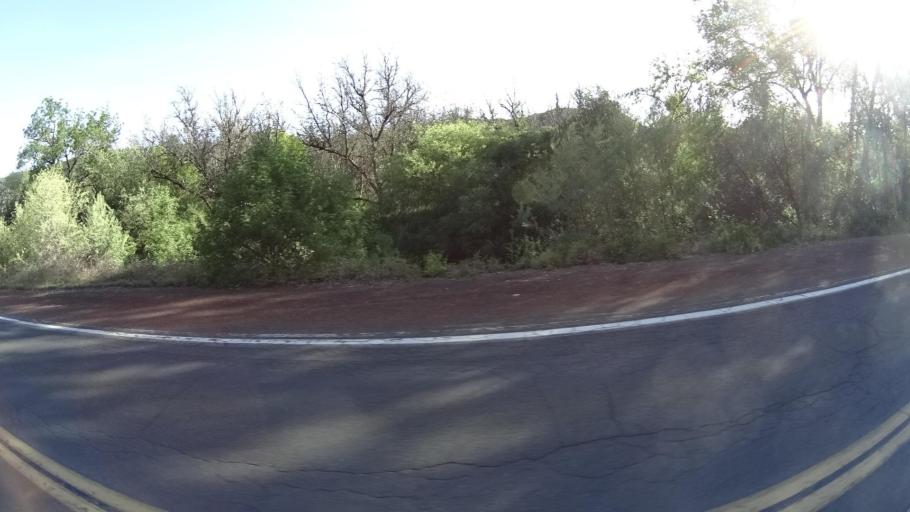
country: US
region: California
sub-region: Lake County
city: North Lakeport
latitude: 39.0923
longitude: -122.9522
